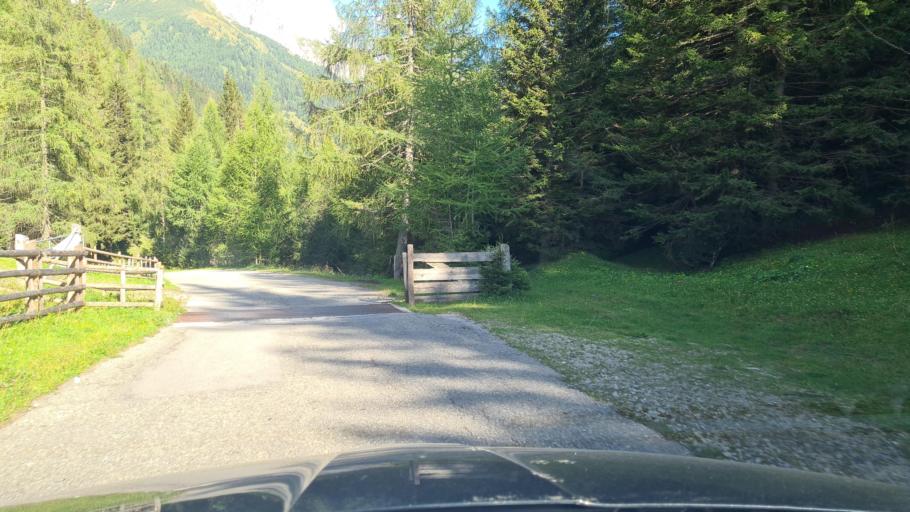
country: AT
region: Salzburg
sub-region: Politischer Bezirk Tamsweg
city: Zederhaus
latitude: 47.1856
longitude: 13.4223
